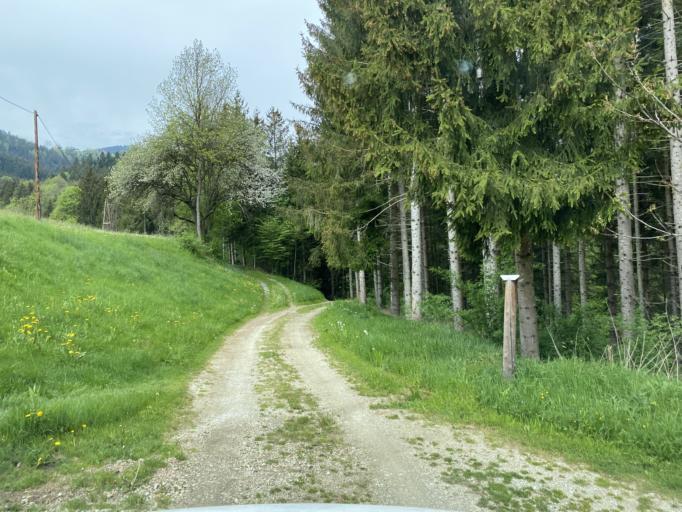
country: AT
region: Styria
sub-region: Politischer Bezirk Weiz
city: Birkfeld
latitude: 47.3399
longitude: 15.6826
